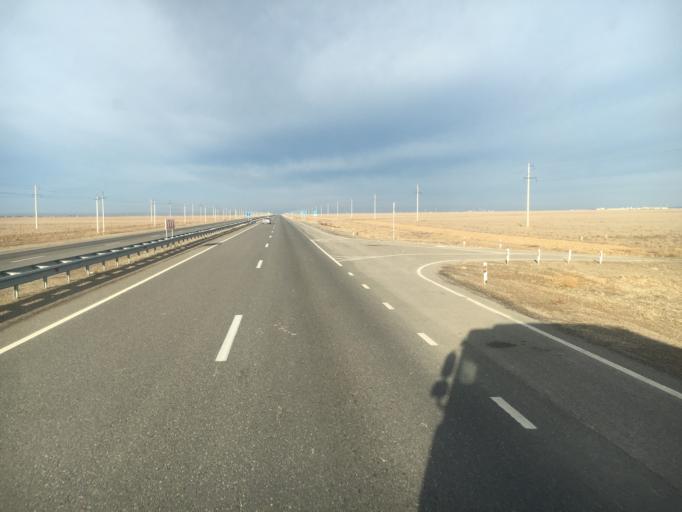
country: KZ
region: Ongtustik Qazaqstan
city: Turkestan
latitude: 43.4279
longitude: 67.9970
